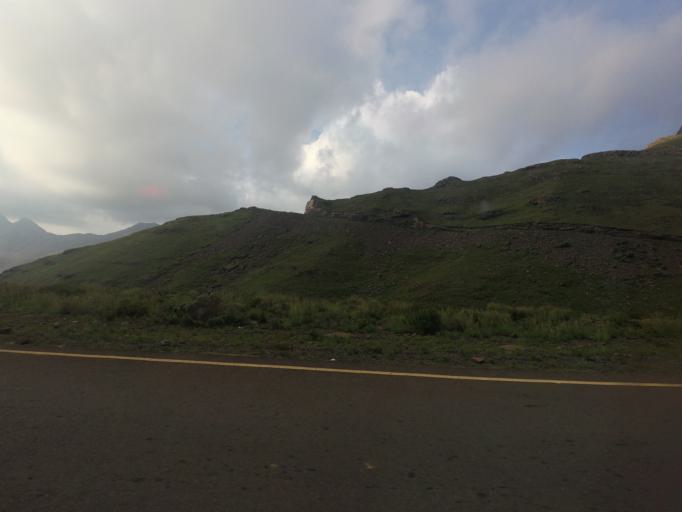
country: LS
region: Butha-Buthe
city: Butha-Buthe
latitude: -29.0723
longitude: 28.3789
